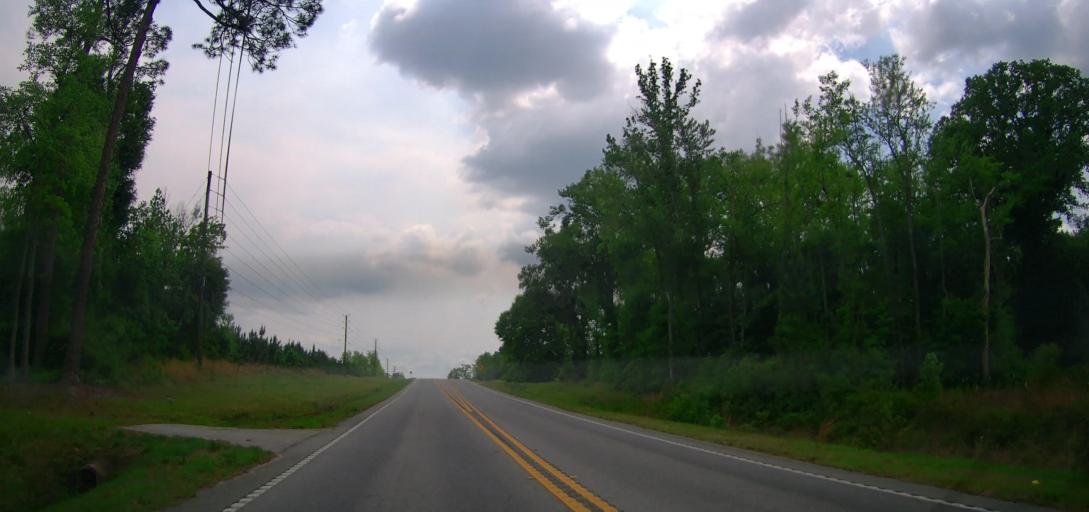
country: US
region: Georgia
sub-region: Treutlen County
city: Soperton
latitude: 32.3625
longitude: -82.5952
